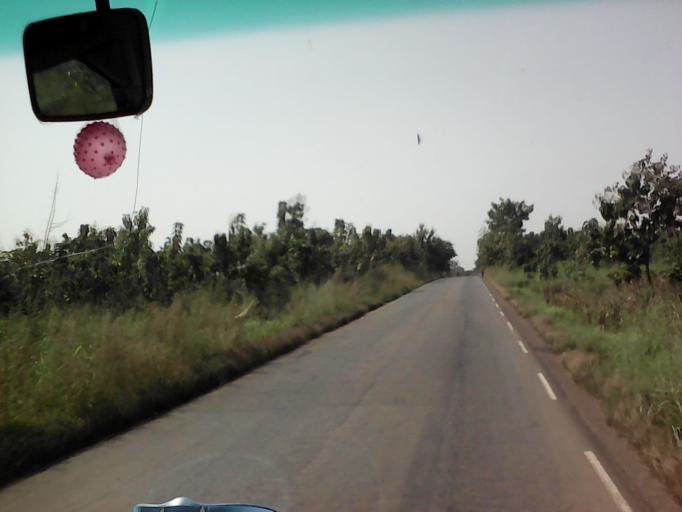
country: TG
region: Centrale
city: Sokode
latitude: 8.8582
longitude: 1.0760
